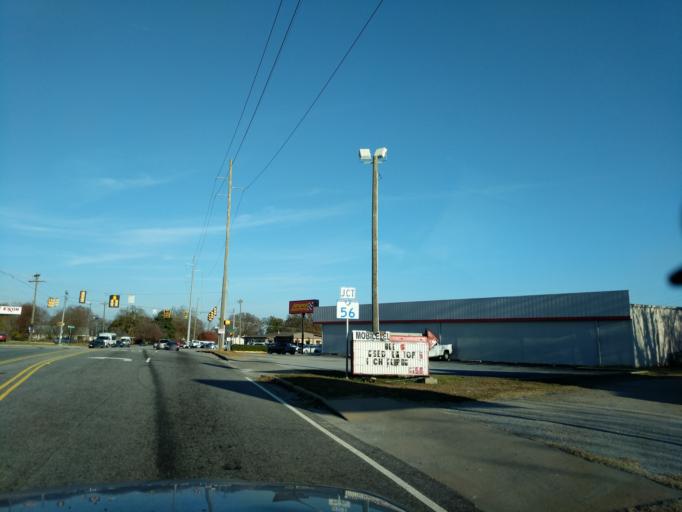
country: US
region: South Carolina
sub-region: Spartanburg County
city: Saxon
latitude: 34.9734
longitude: -81.9600
